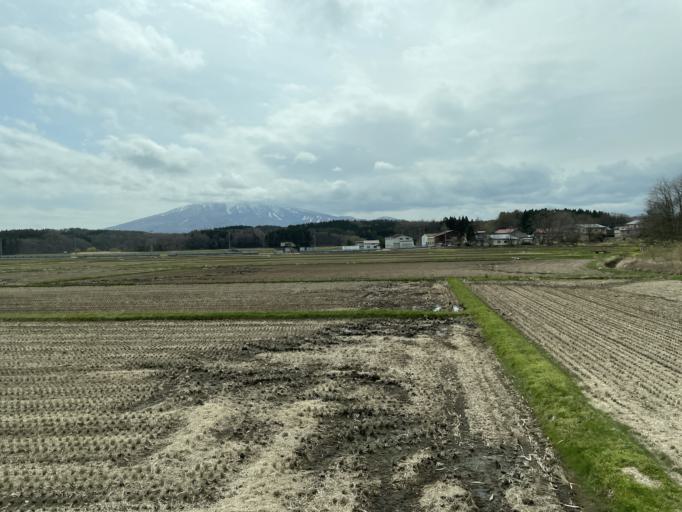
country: JP
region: Aomori
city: Shimokizukuri
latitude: 40.7859
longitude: 140.3113
